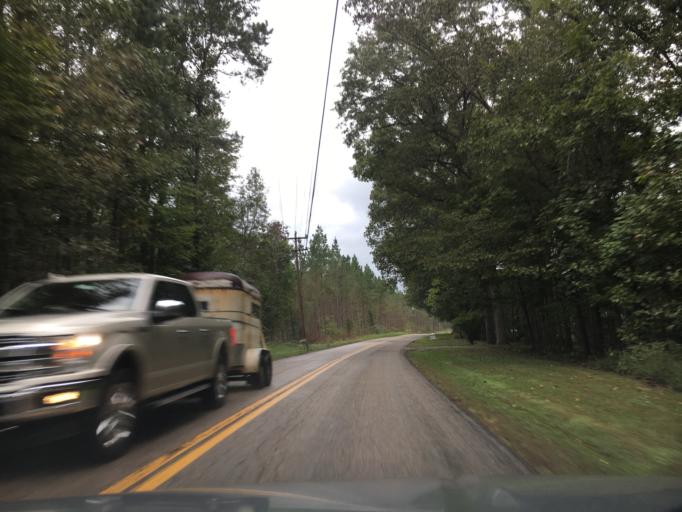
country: US
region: Virginia
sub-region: Amelia County
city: Amelia Court House
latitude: 37.3644
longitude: -77.9763
